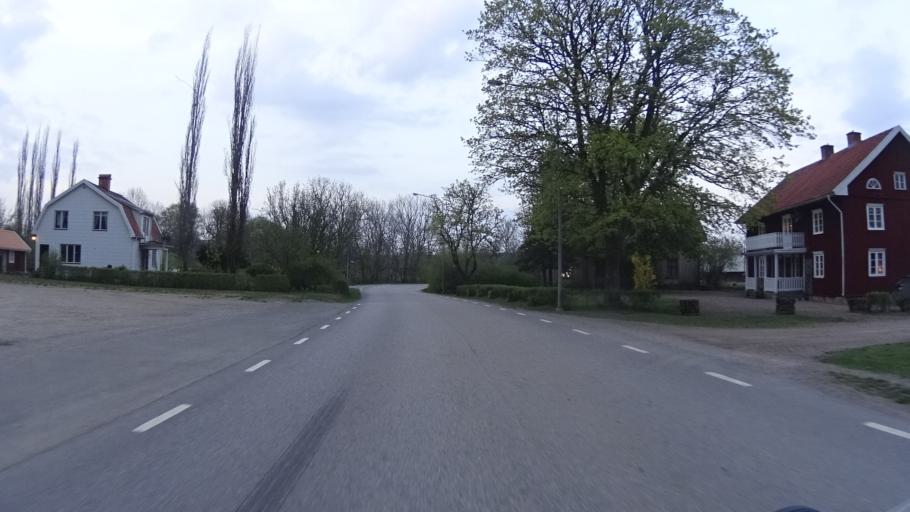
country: SE
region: Vaestra Goetaland
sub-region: Gotene Kommun
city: Kallby
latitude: 58.5599
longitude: 13.3501
